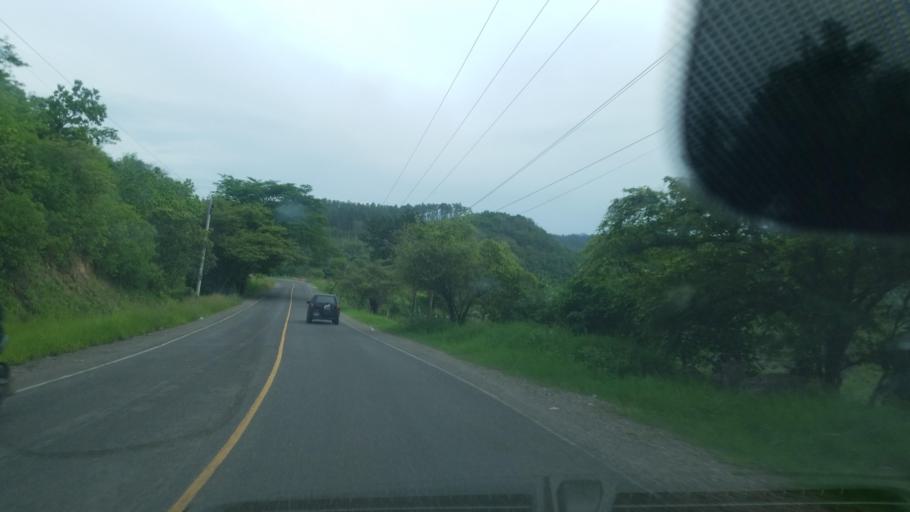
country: HN
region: Santa Barbara
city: Santa Barbara
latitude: 14.9167
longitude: -88.2512
